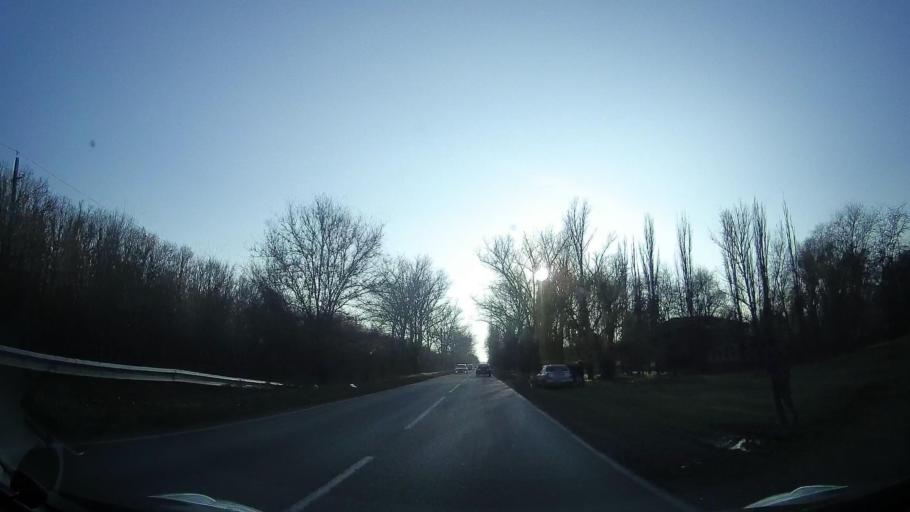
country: RU
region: Rostov
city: Ol'ginskaya
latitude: 47.1722
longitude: 39.9467
